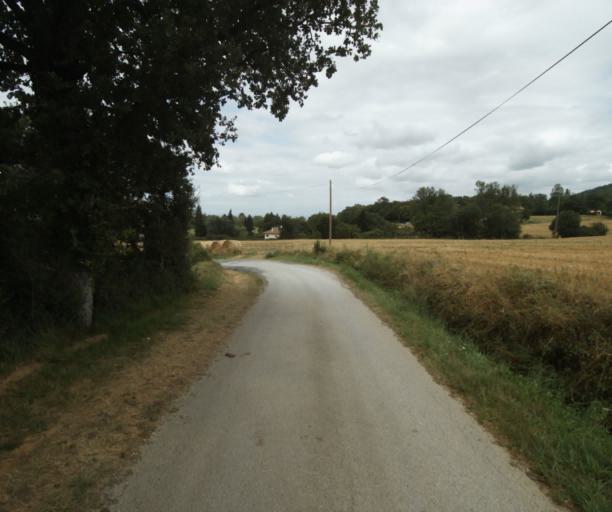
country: FR
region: Midi-Pyrenees
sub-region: Departement du Tarn
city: Soreze
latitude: 43.4562
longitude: 2.0792
